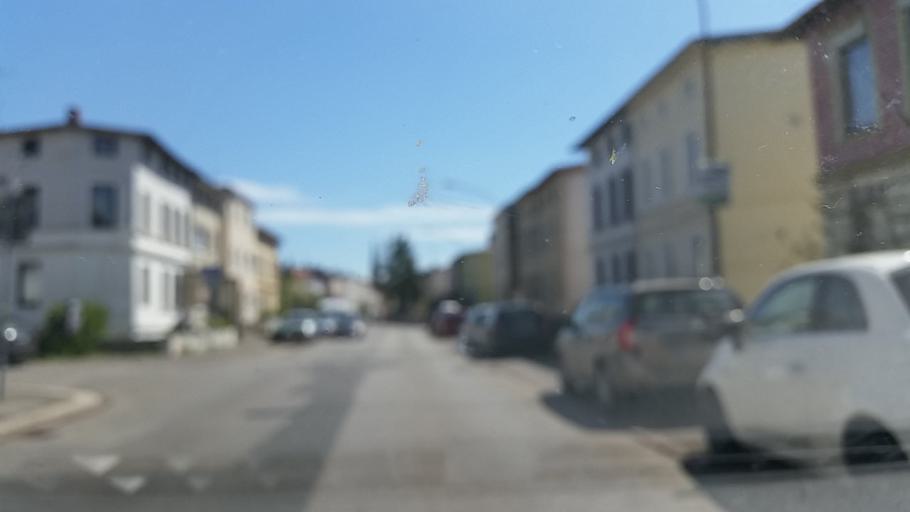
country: DE
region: Schleswig-Holstein
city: Luebeck
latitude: 53.8761
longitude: 10.6696
